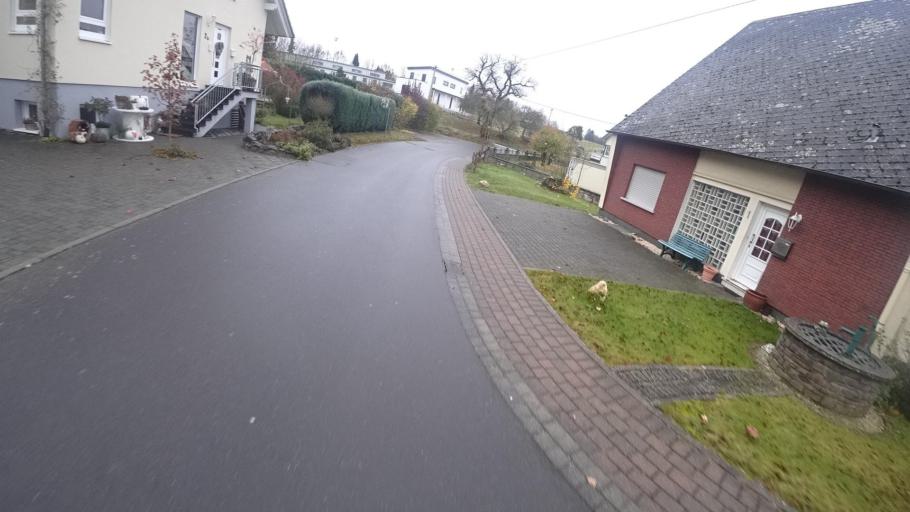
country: DE
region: Rheinland-Pfalz
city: Leiningen
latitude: 50.1312
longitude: 7.5731
